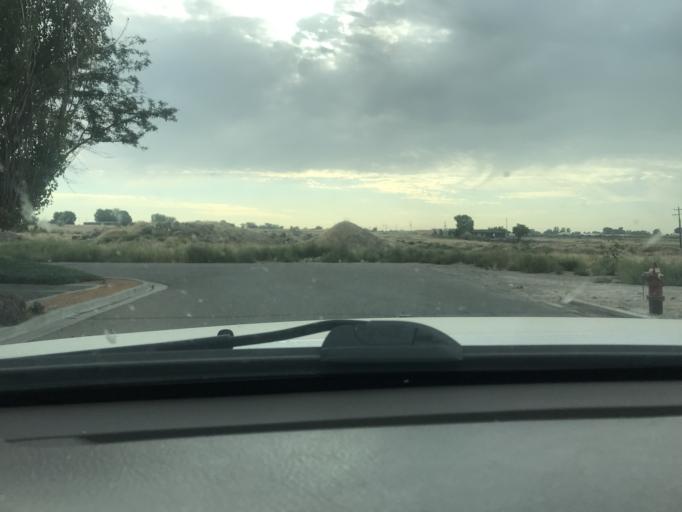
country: US
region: Idaho
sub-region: Jerome County
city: Jerome
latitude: 42.6921
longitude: -114.5171
